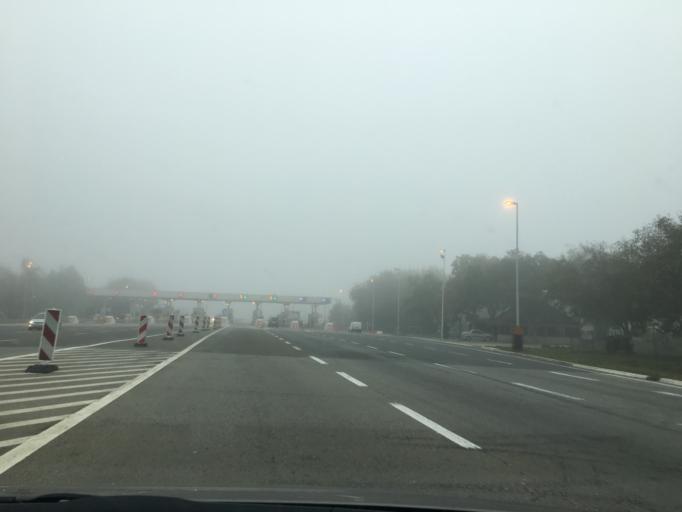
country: RS
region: Autonomna Pokrajina Vojvodina
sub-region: Sremski Okrug
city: Stara Pazova
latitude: 45.0054
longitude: 20.2021
